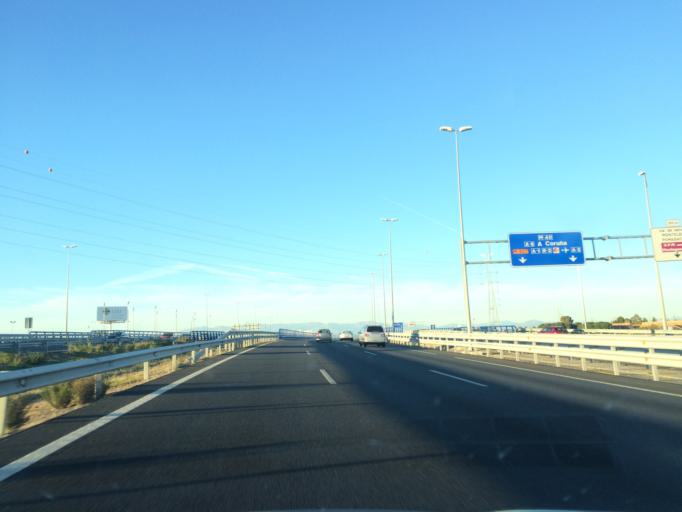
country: ES
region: Madrid
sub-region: Provincia de Madrid
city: Pozuelo de Alarcon
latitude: 40.3956
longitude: -3.8328
